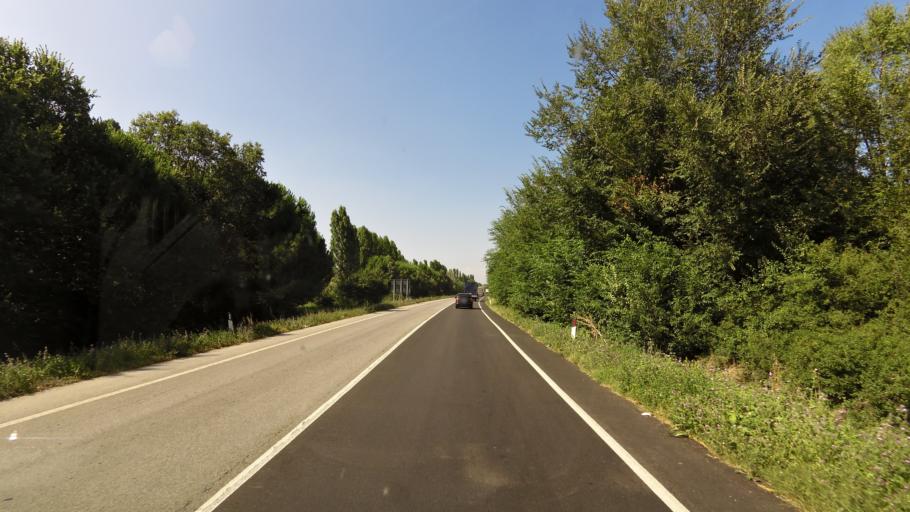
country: IT
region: Emilia-Romagna
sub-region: Provincia di Ravenna
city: Ravenna
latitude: 44.4729
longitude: 12.2095
